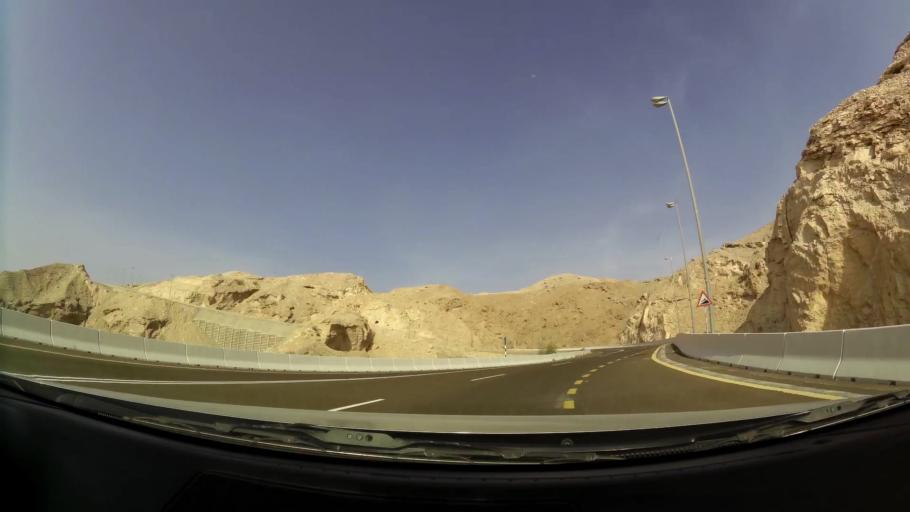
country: AE
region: Abu Dhabi
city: Al Ain
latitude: 24.0949
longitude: 55.7581
